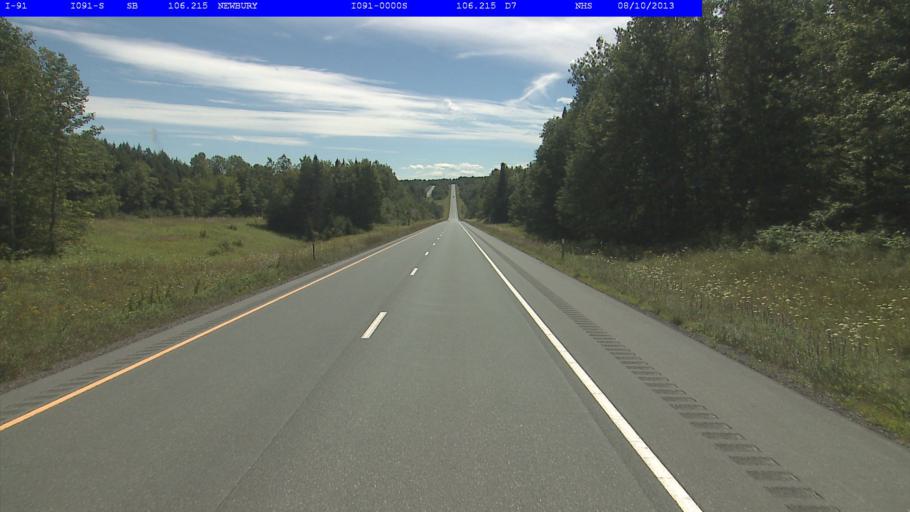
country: US
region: New Hampshire
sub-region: Grafton County
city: Haverhill
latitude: 44.1035
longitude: -72.1094
